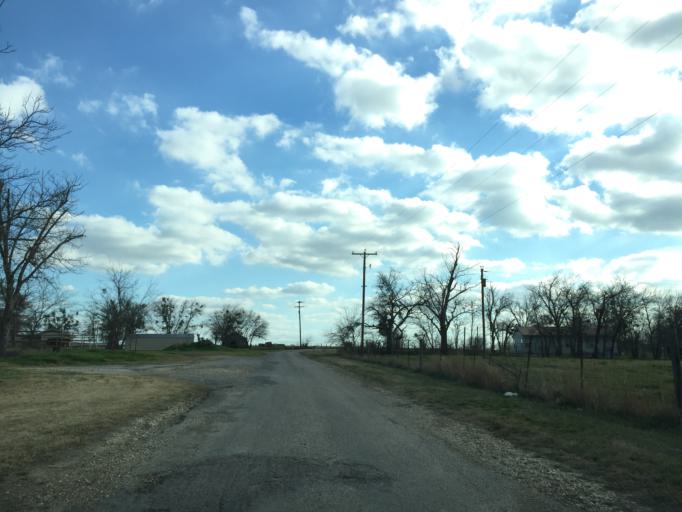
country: US
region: Texas
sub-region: Williamson County
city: Taylor
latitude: 30.6326
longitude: -97.4354
